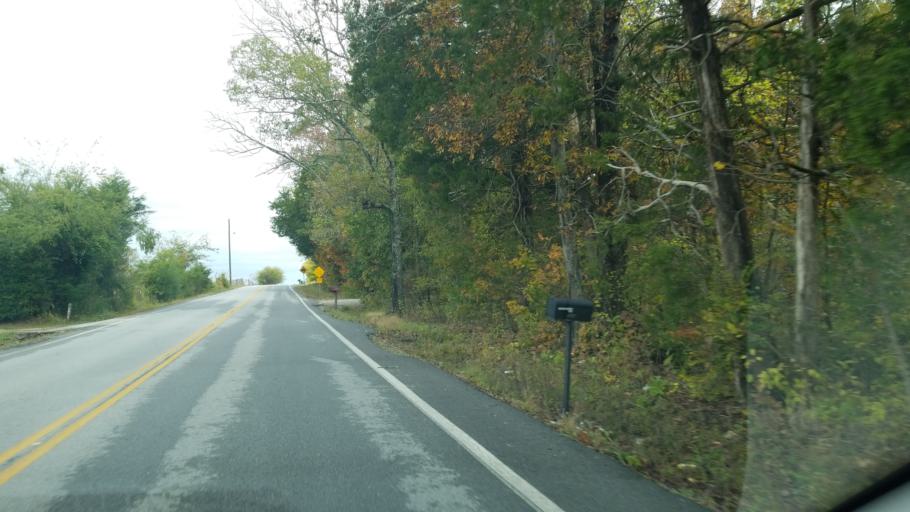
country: US
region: Tennessee
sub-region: Hamilton County
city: Lakesite
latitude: 35.1780
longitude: -85.0263
